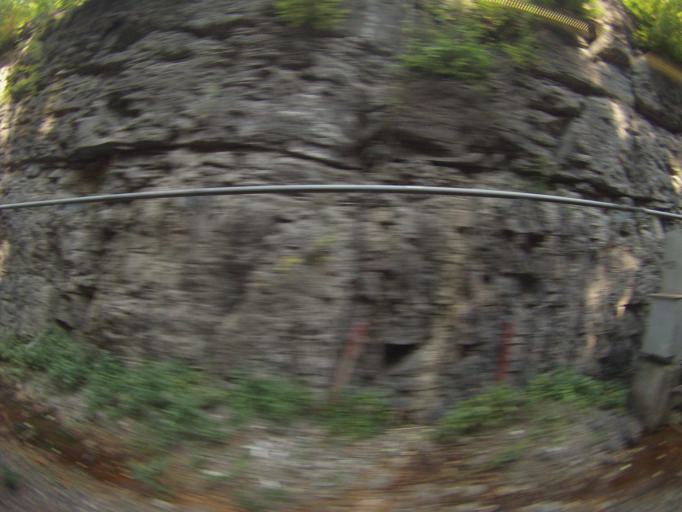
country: CA
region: Ontario
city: Ottawa
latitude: 45.3935
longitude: -75.7061
